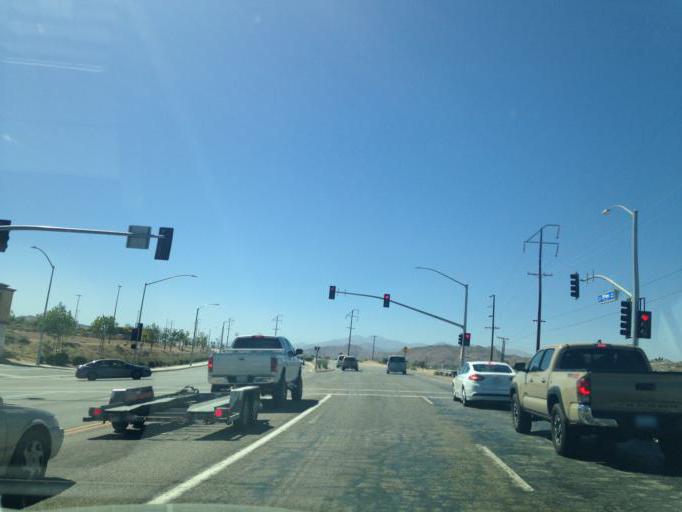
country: US
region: California
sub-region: San Bernardino County
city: Yucca Valley
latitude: 34.1350
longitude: -116.3825
